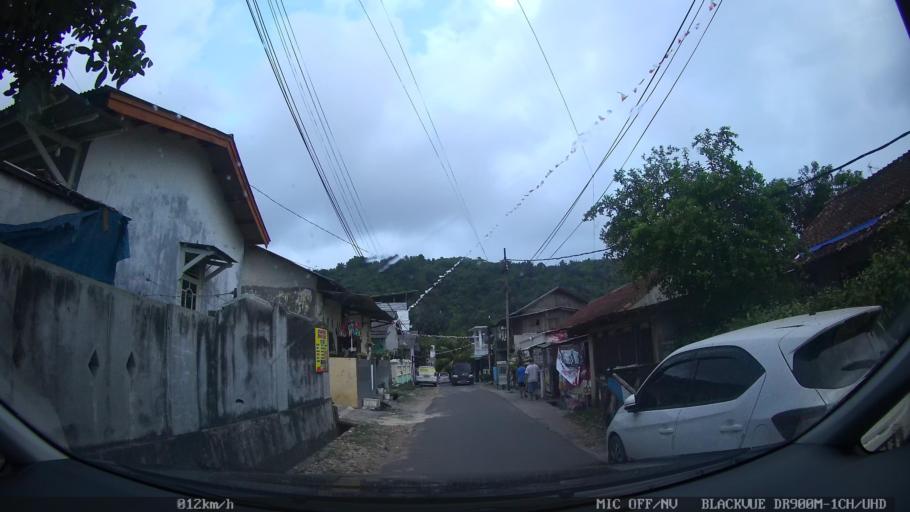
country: ID
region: Lampung
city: Bandarlampung
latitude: -5.4239
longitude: 105.2782
